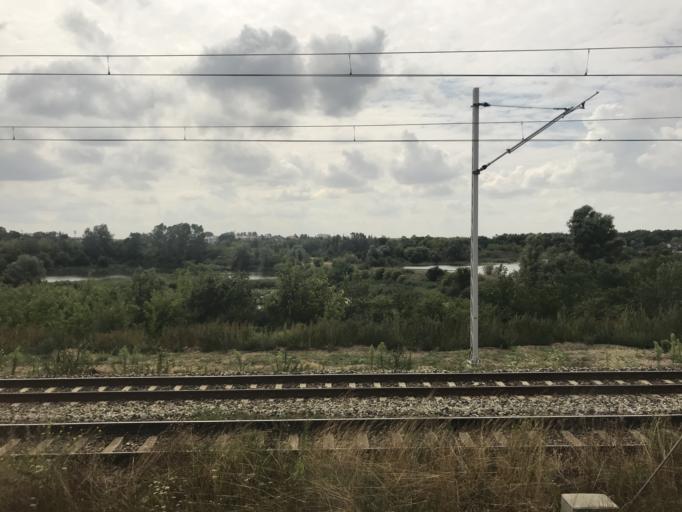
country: PL
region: Greater Poland Voivodeship
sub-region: Powiat gnieznienski
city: Gniezno
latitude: 52.5276
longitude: 17.5877
